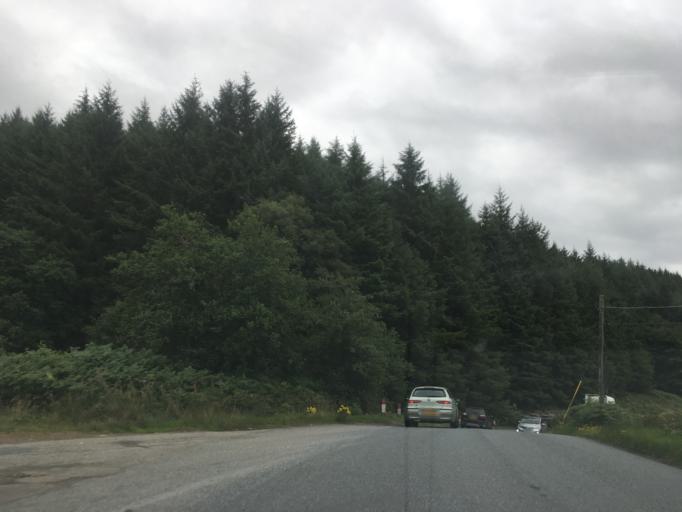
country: GB
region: Scotland
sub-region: Argyll and Bute
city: Oban
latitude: 56.2750
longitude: -5.4780
